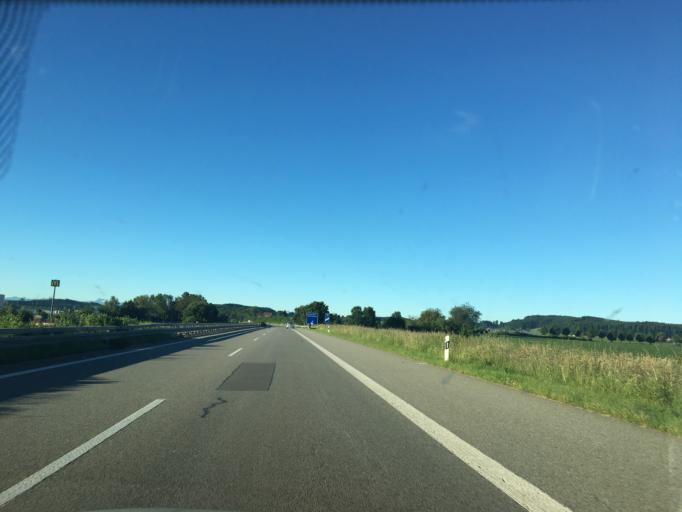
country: DE
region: Bavaria
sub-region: Swabia
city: Wolfertschwenden
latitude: 47.8861
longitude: 10.2459
